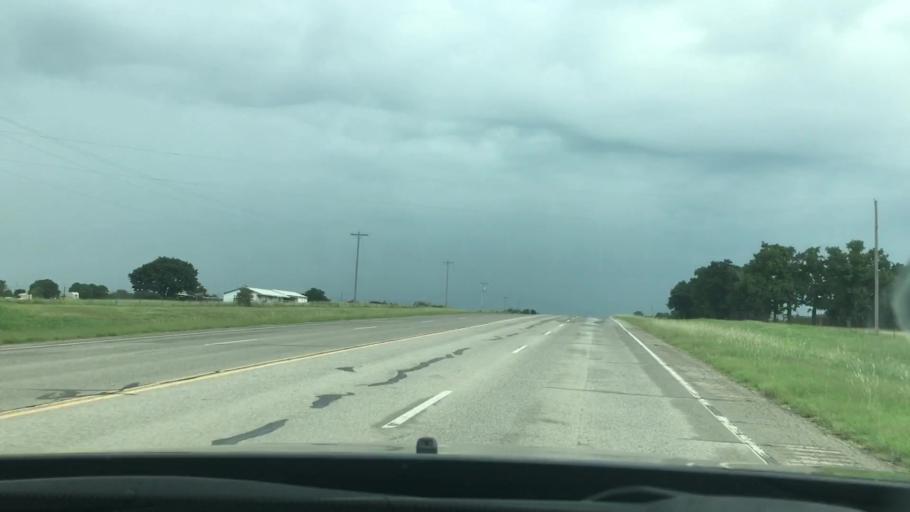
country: US
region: Oklahoma
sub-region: Carter County
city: Healdton
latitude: 34.1907
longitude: -97.4747
